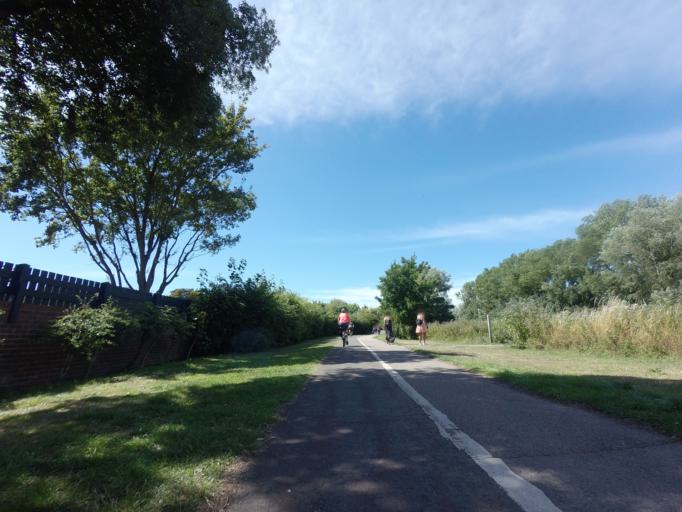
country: GB
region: England
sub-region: Kent
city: Sandwich
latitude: 51.2738
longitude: 1.3479
